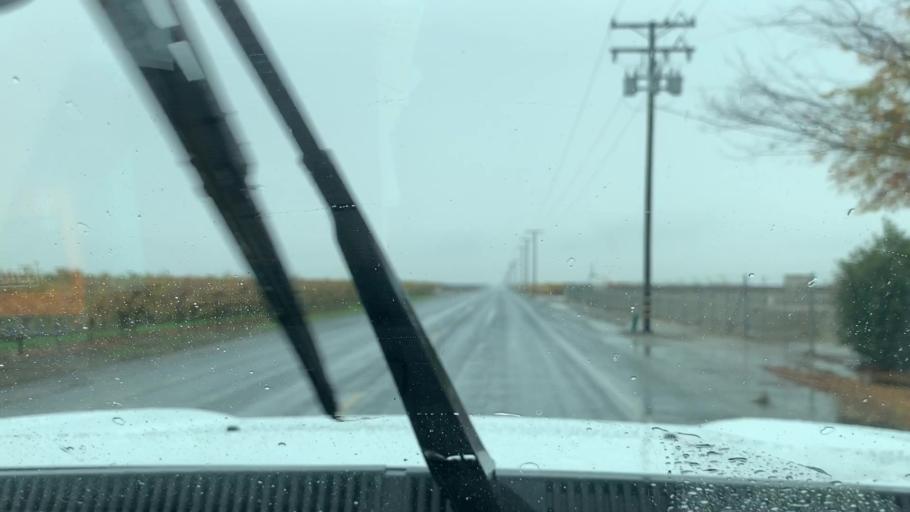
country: US
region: California
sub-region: Tulare County
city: Earlimart
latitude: 35.8919
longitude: -119.2800
